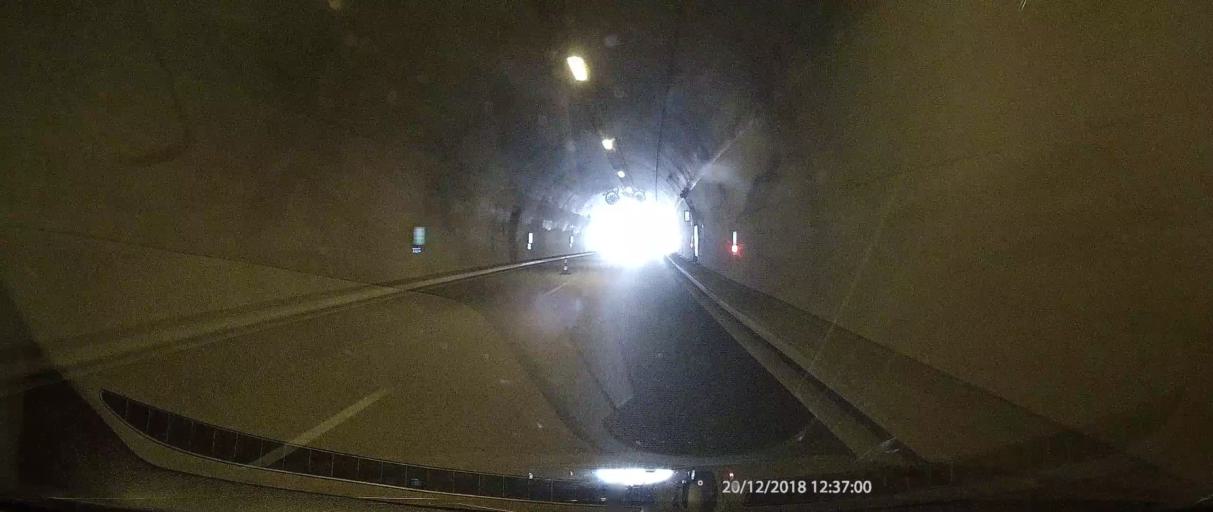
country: GR
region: West Greece
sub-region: Nomos Aitolias kai Akarnanias
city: Antirrio
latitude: 38.3559
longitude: 21.6672
